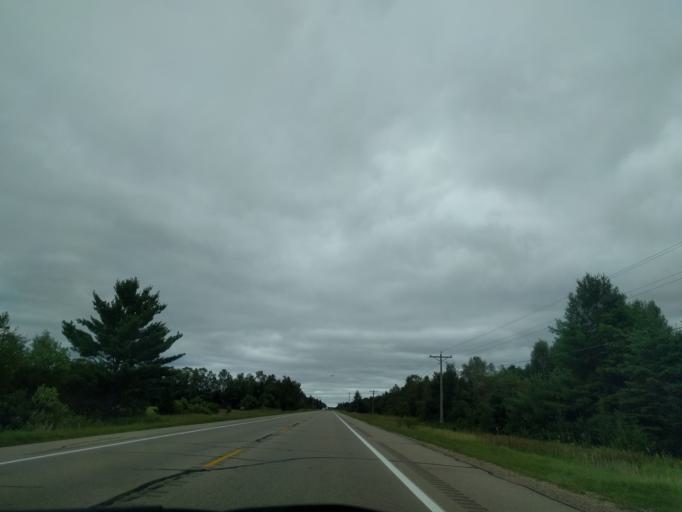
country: US
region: Michigan
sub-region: Delta County
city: Gladstone
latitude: 45.8898
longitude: -87.0659
